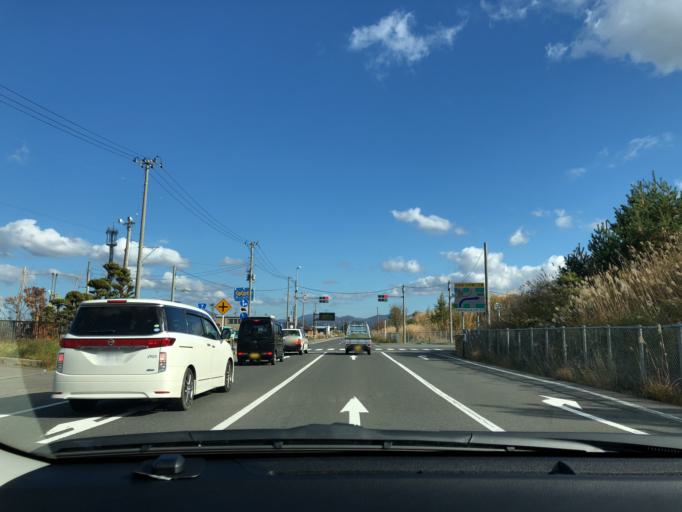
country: JP
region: Aomori
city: Aomori Shi
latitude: 40.7980
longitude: 140.7183
